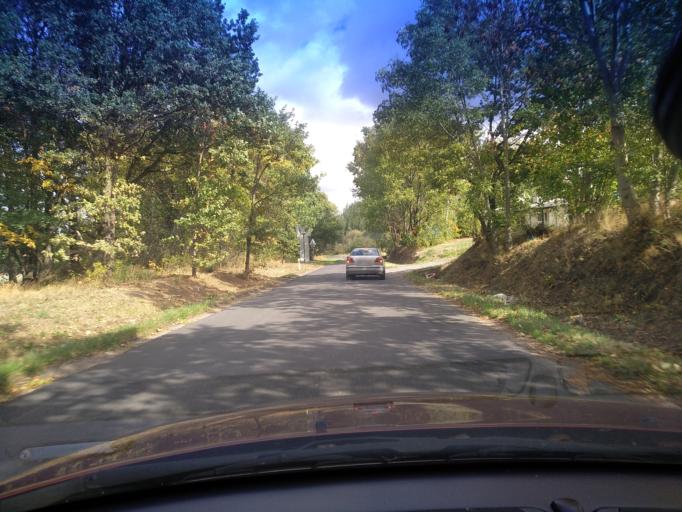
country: PL
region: Lower Silesian Voivodeship
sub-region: Powiat zgorzelecki
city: Zgorzelec
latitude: 51.1724
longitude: 15.0097
